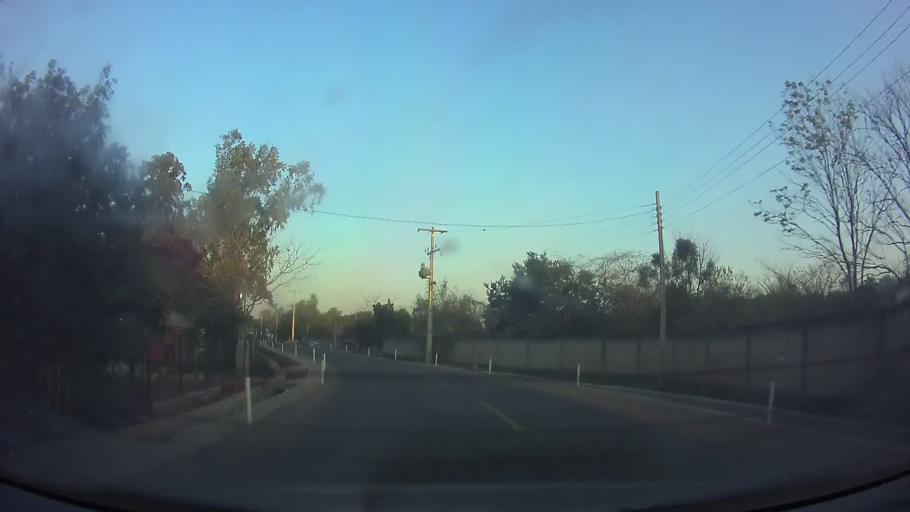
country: PY
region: Central
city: Limpio
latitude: -25.2443
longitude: -57.4934
